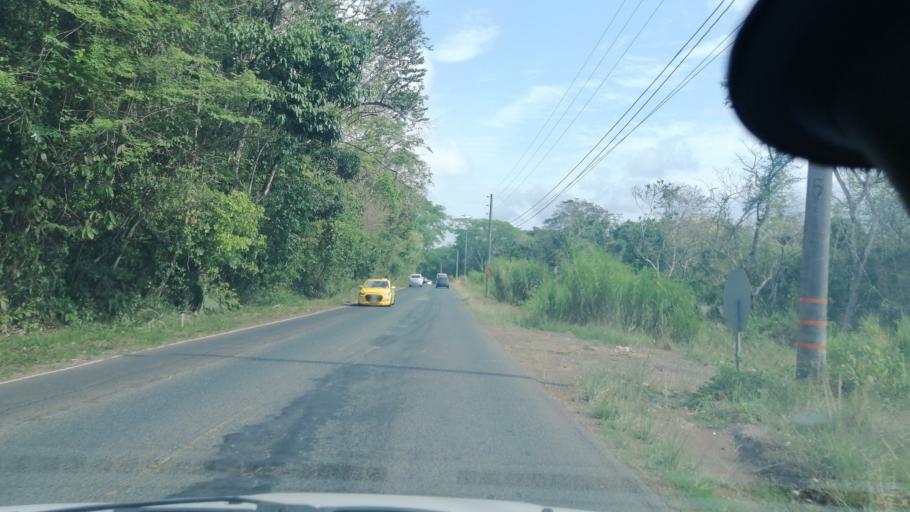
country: PA
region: Panama
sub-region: Distrito de Panama
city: Paraiso
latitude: 9.0422
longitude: -79.6347
